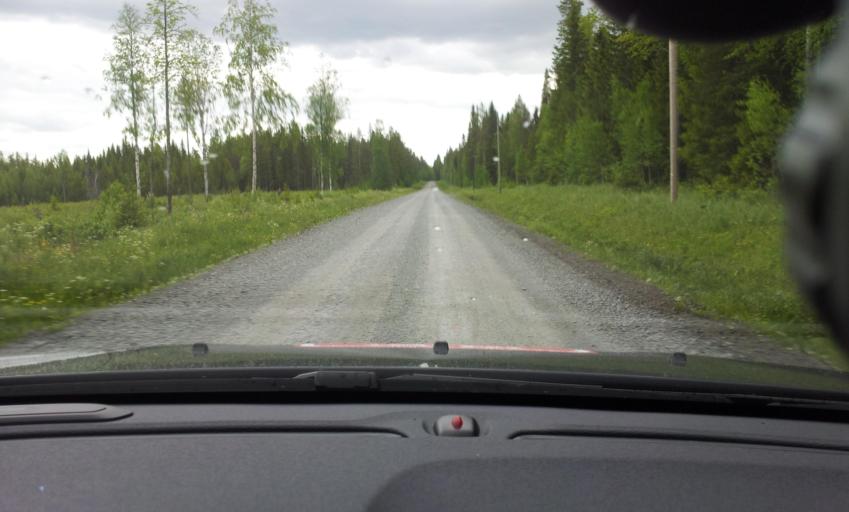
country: SE
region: Jaemtland
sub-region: OEstersunds Kommun
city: Brunflo
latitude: 63.1695
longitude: 14.9825
